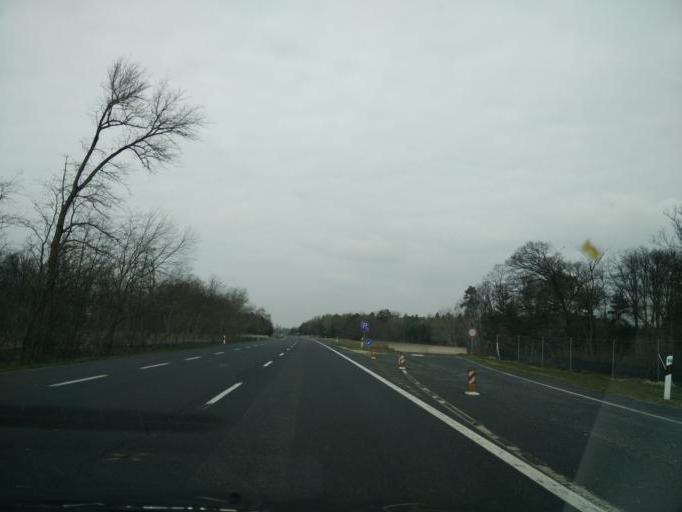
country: HU
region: Gyor-Moson-Sopron
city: Toltestava
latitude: 47.7095
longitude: 17.7490
